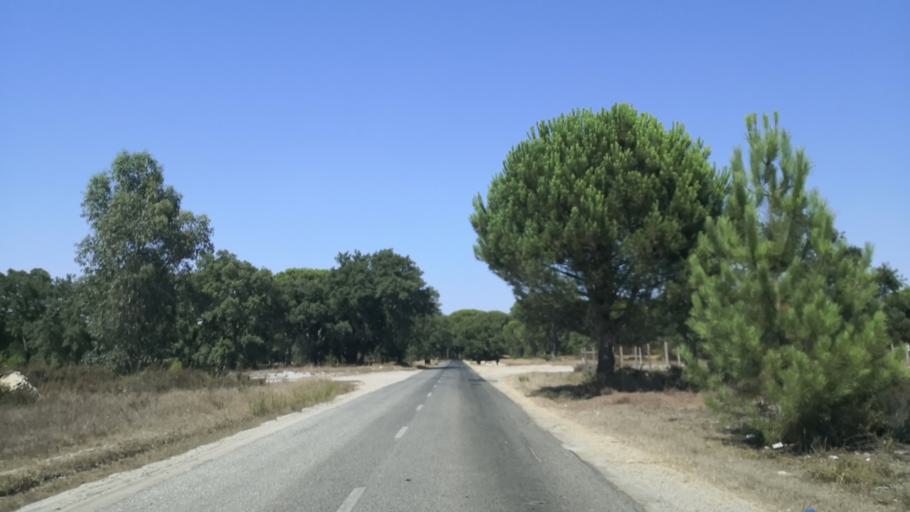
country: PT
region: Santarem
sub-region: Benavente
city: Poceirao
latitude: 38.7334
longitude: -8.7001
